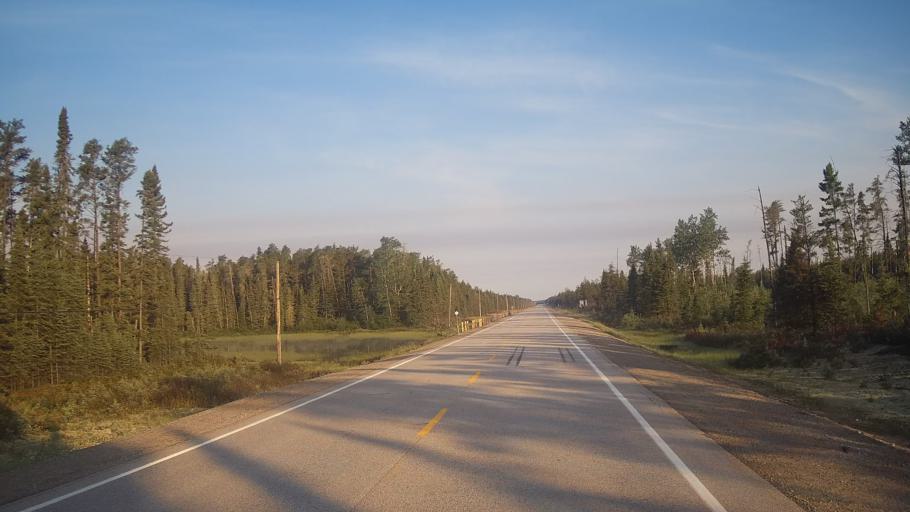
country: CA
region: Ontario
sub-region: Rainy River District
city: Atikokan
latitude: 49.2372
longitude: -90.9892
